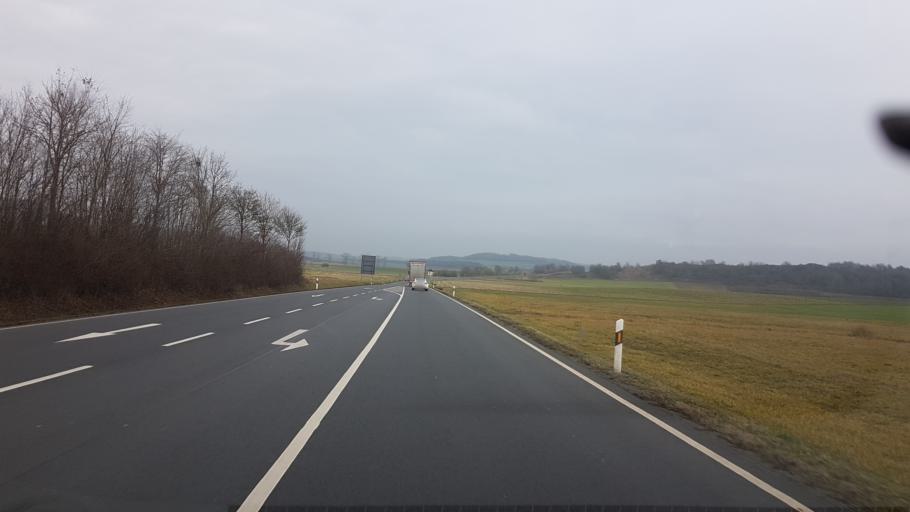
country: DE
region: Bavaria
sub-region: Regierungsbezirk Unterfranken
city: Bad Konigshofen im Grabfeld
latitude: 50.2794
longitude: 10.5008
